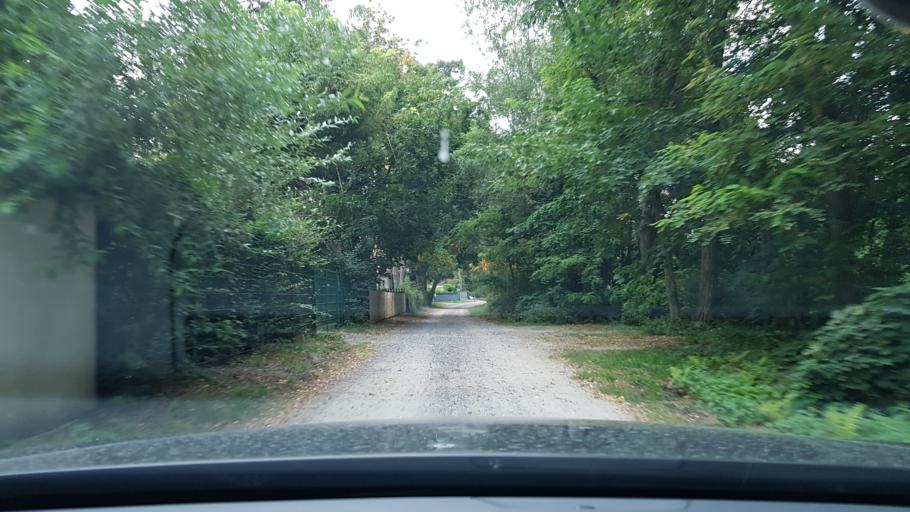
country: DE
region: Berlin
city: Mahlsdorf
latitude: 52.4827
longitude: 13.6298
